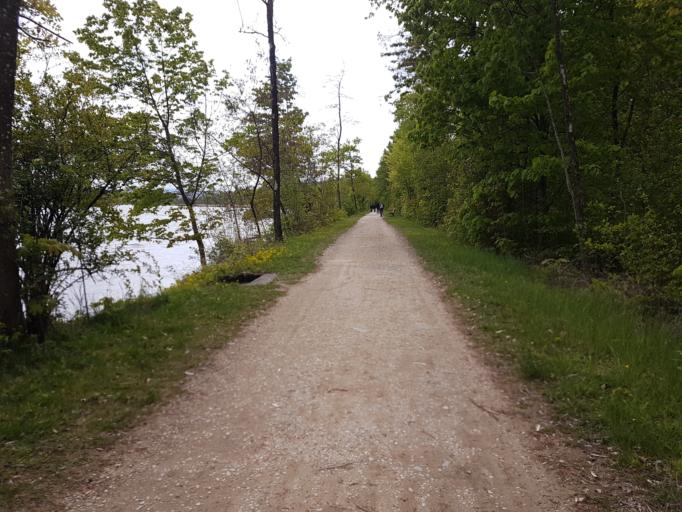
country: CH
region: Aargau
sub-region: Bezirk Brugg
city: Schinznach Bad
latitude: 47.4374
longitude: 8.1629
